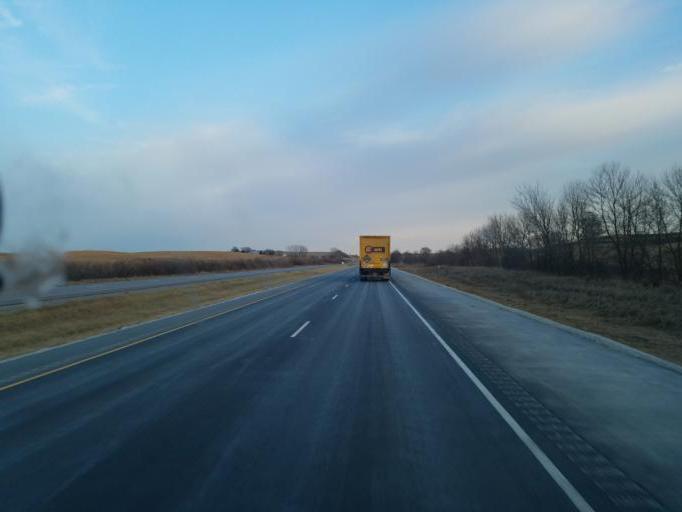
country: US
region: Iowa
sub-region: Harrison County
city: Logan
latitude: 41.4981
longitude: -95.6788
